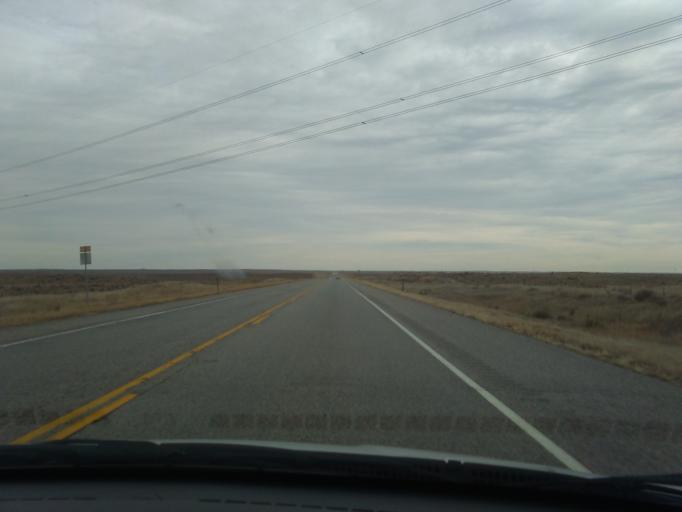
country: US
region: Colorado
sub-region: Morgan County
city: Brush
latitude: 40.2558
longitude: -103.5125
